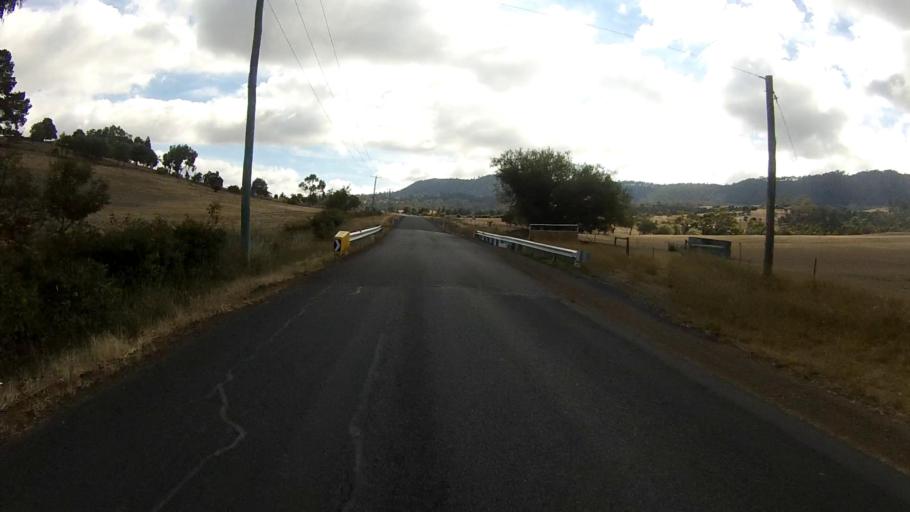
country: AU
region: Tasmania
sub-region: Brighton
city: Old Beach
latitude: -42.7678
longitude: 147.2972
